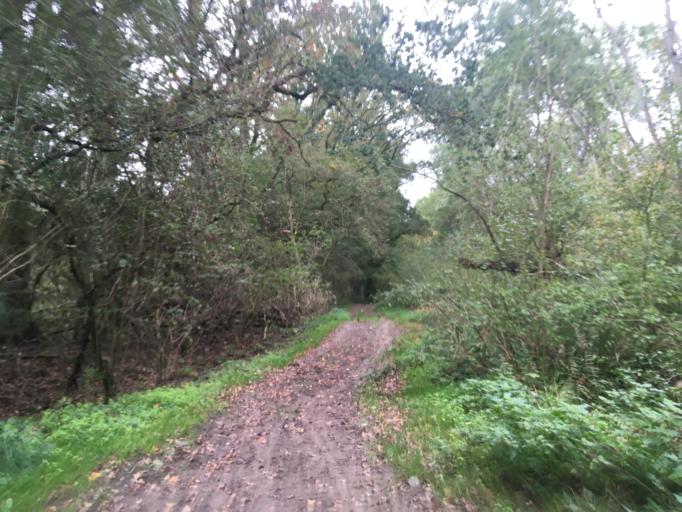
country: DE
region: Brandenburg
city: Falkensee
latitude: 52.5197
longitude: 13.0976
